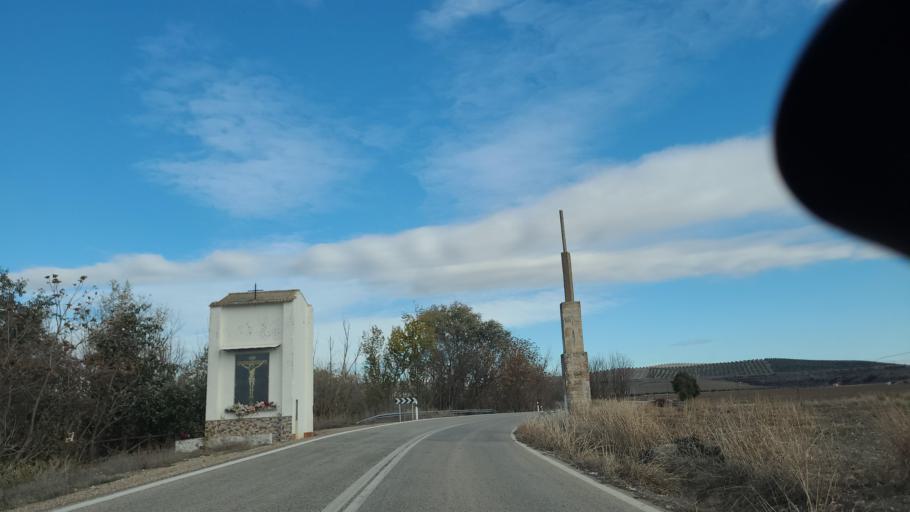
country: ES
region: Andalusia
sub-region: Provincia de Jaen
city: Villanueva de la Reina
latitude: 38.0107
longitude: -3.8999
